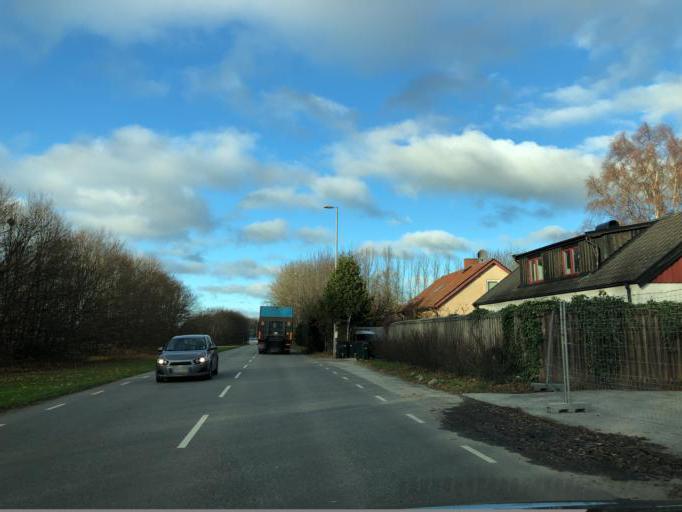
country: SE
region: Skane
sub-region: Lunds Kommun
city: Lund
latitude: 55.7262
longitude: 13.1810
